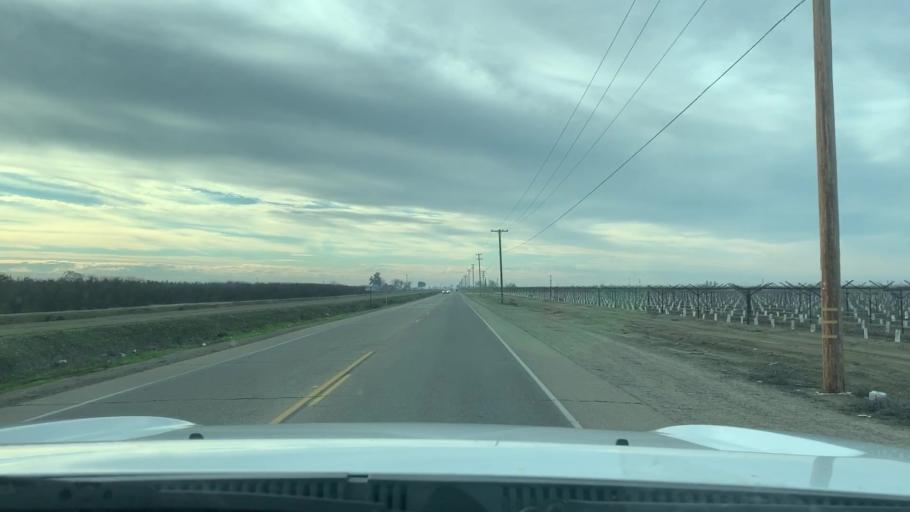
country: US
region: California
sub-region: Fresno County
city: Fowler
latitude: 36.6055
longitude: -119.7013
